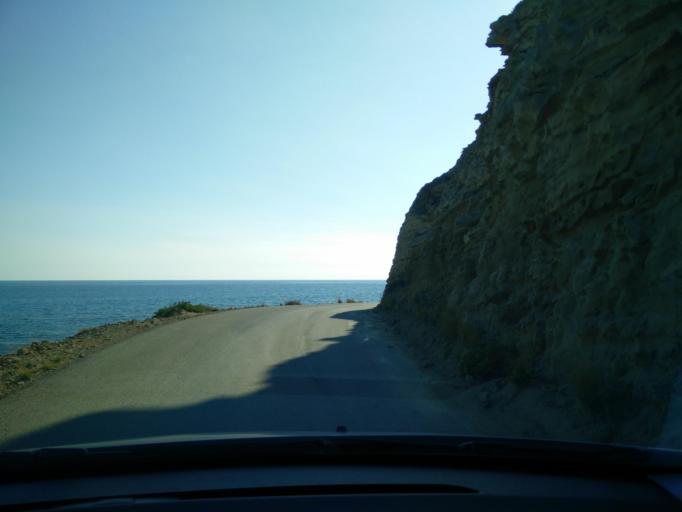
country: GR
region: Crete
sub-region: Nomos Lasithiou
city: Gra Liyia
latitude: 34.9939
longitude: 25.5541
